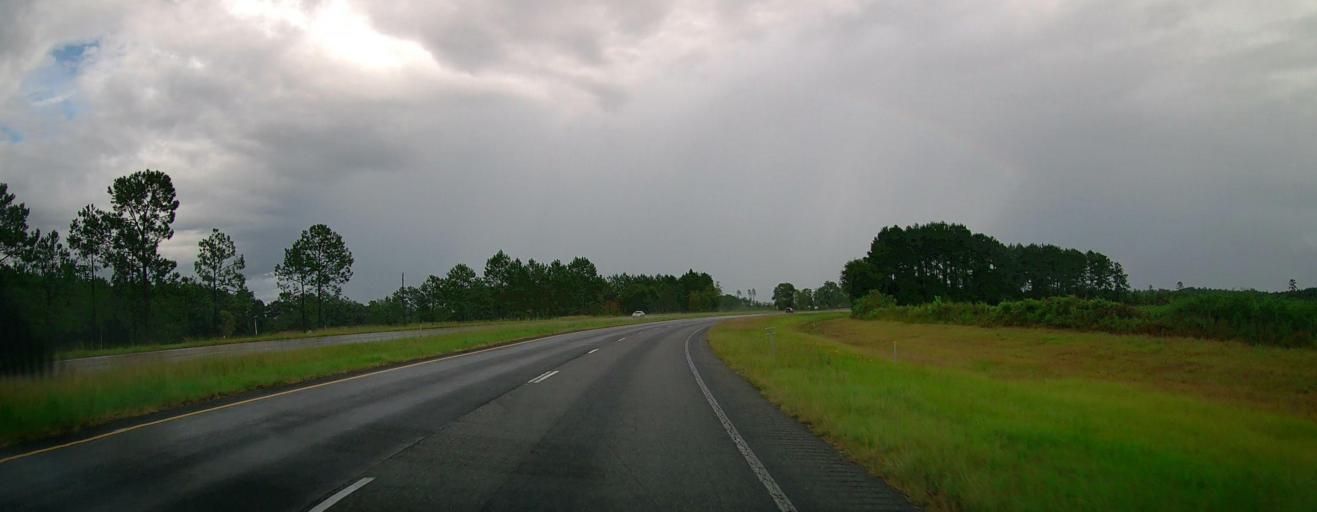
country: US
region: Georgia
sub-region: Ware County
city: Deenwood
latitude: 31.2565
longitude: -82.4655
